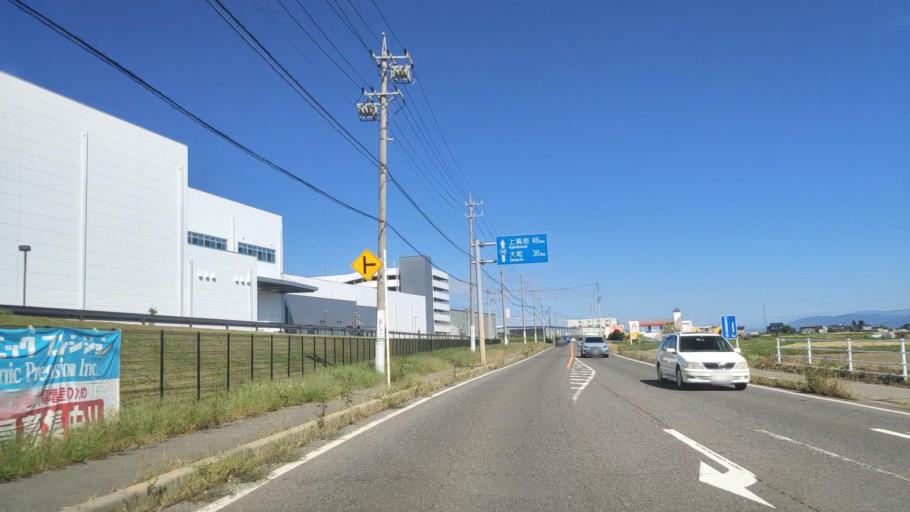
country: JP
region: Nagano
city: Matsumoto
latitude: 36.1873
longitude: 137.9034
